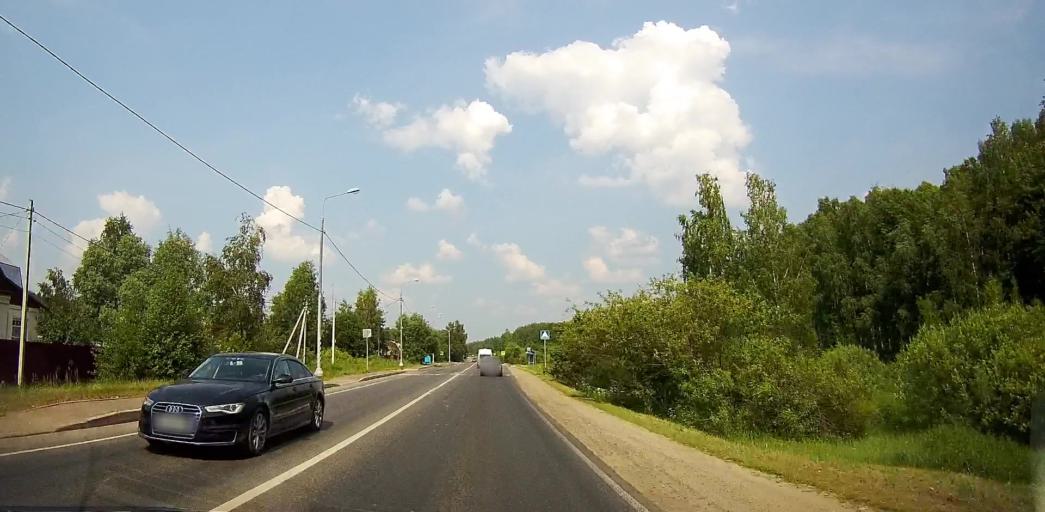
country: RU
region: Moskovskaya
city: Stupino
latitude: 54.9163
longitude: 38.1038
